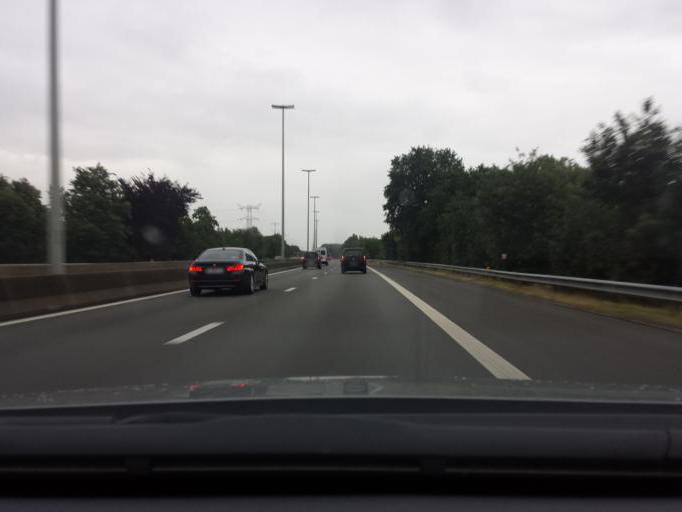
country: BE
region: Flanders
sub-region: Provincie Antwerpen
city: Nijlen
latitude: 51.1817
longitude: 4.6871
